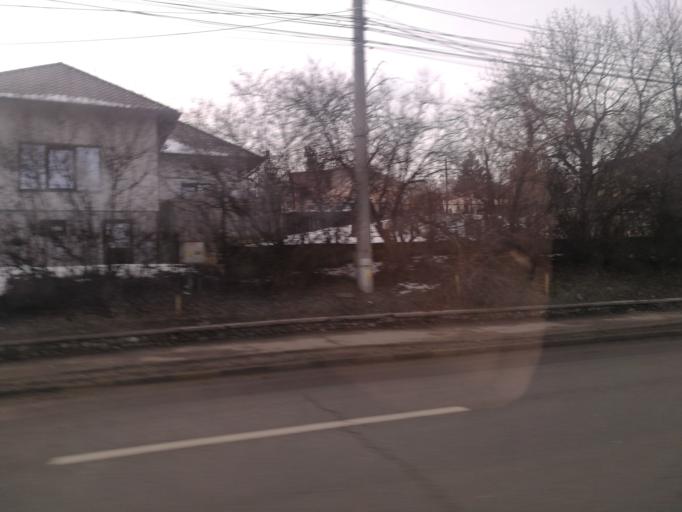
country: RO
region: Suceava
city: Suceava
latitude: 47.6510
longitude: 26.2608
